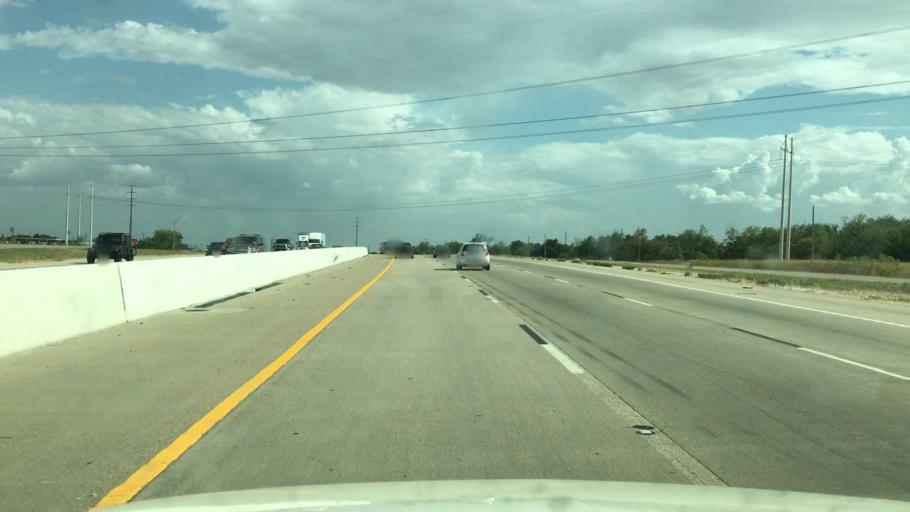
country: US
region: Texas
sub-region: McLennan County
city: Northcrest
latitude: 31.7019
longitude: -97.1024
